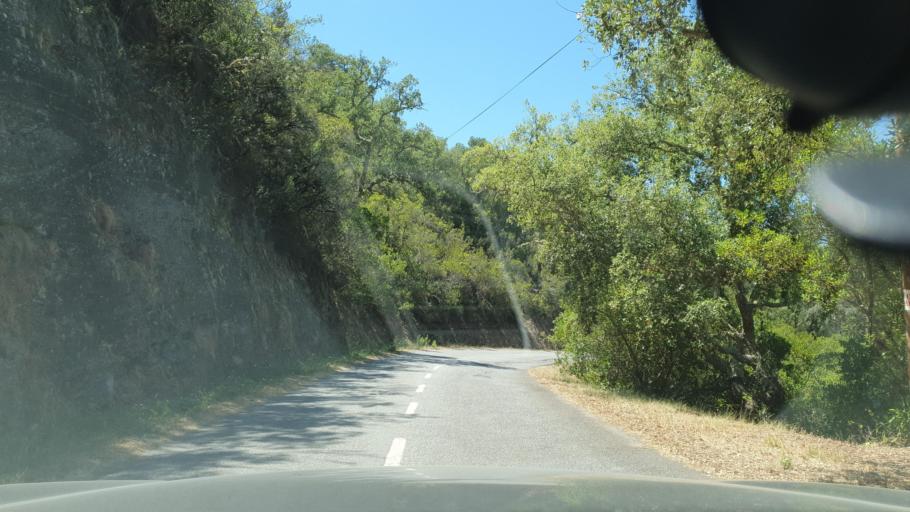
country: PT
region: Beja
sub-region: Odemira
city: Odemira
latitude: 37.6026
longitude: -8.5730
